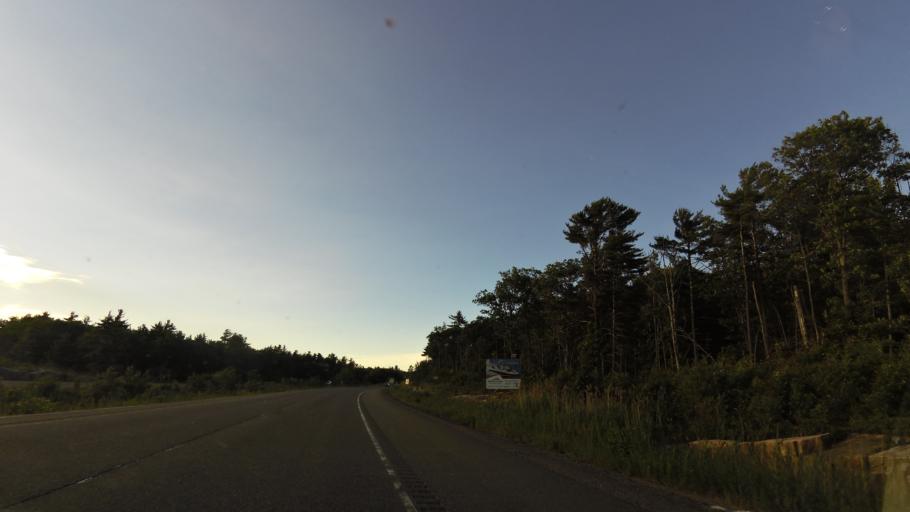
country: CA
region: Ontario
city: Midland
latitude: 44.8106
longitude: -79.7395
